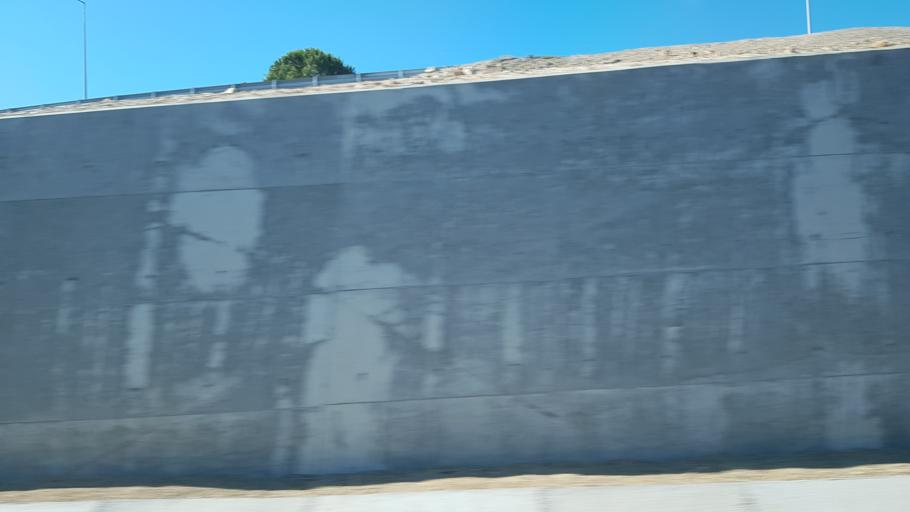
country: TR
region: Istanbul
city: Silivri
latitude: 41.1212
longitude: 28.1890
